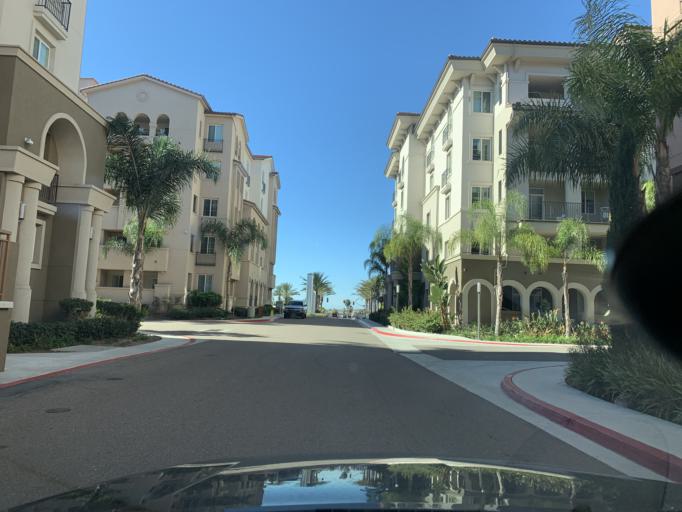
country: US
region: California
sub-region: San Diego County
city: Poway
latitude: 32.9220
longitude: -117.1168
